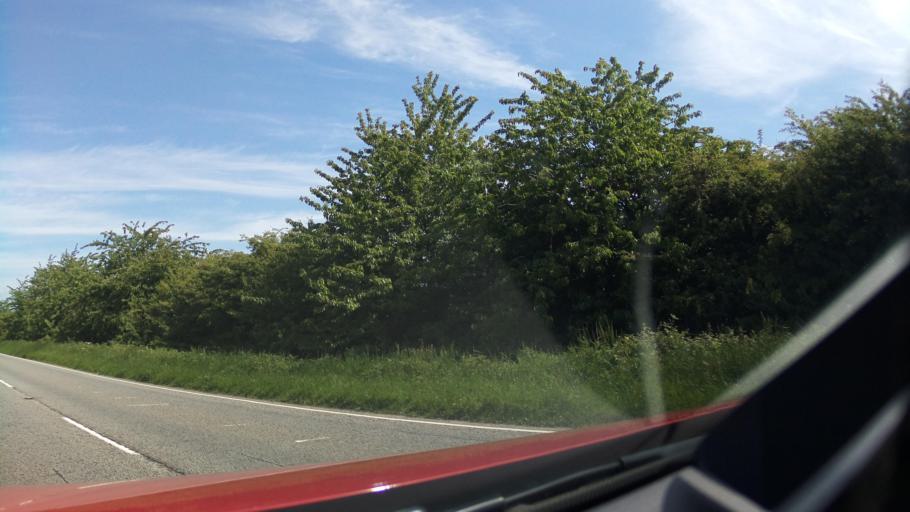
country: GB
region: England
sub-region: Lincolnshire
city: Dunholme
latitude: 53.3759
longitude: -0.5466
